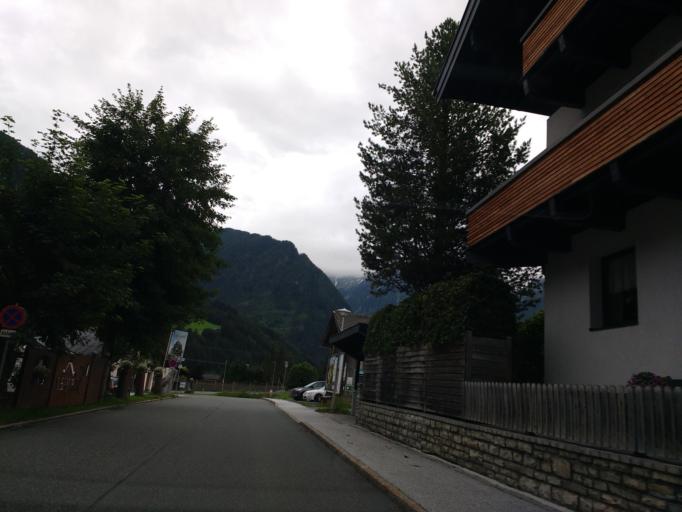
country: AT
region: Salzburg
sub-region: Politischer Bezirk Zell am See
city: Neukirchen am Grossvenediger
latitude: 47.2500
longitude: 12.2736
